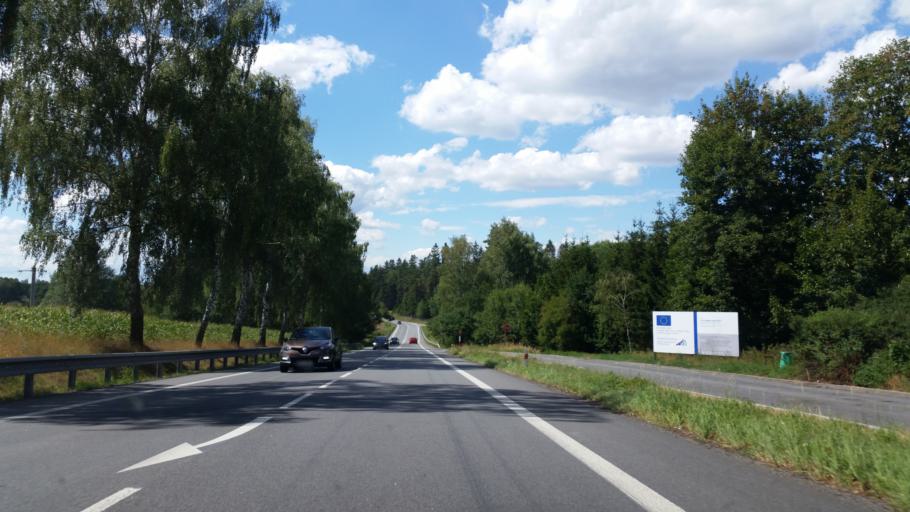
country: CZ
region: Vysocina
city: Pacov
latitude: 49.4253
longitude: 15.0369
